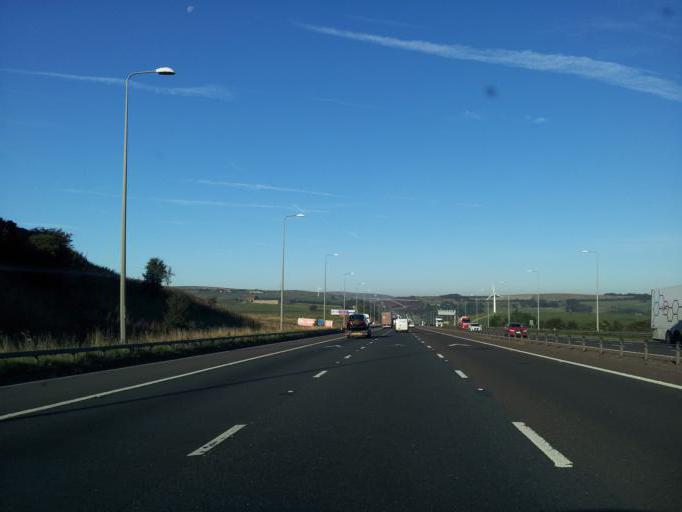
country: GB
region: England
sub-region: Kirklees
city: Marsden
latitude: 53.6445
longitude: -1.9048
